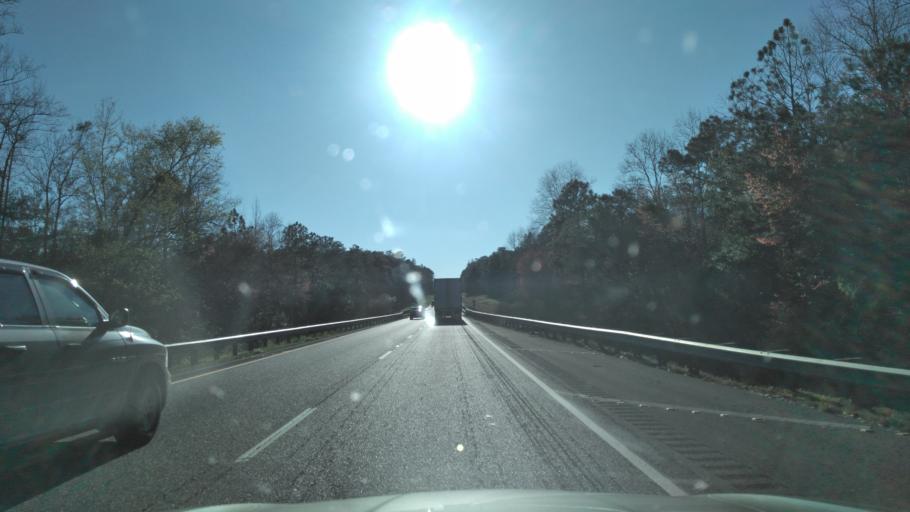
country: US
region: Alabama
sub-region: Escambia County
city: Atmore
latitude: 31.0647
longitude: -87.5657
